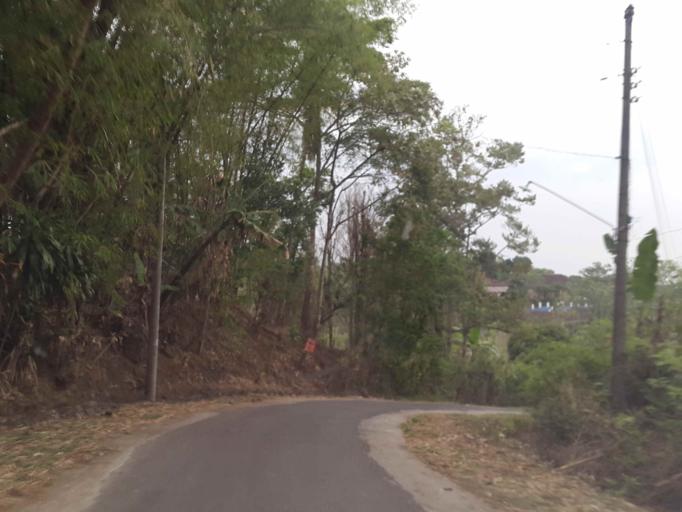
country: ID
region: Central Java
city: Jatiroto
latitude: -7.7294
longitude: 111.0669
